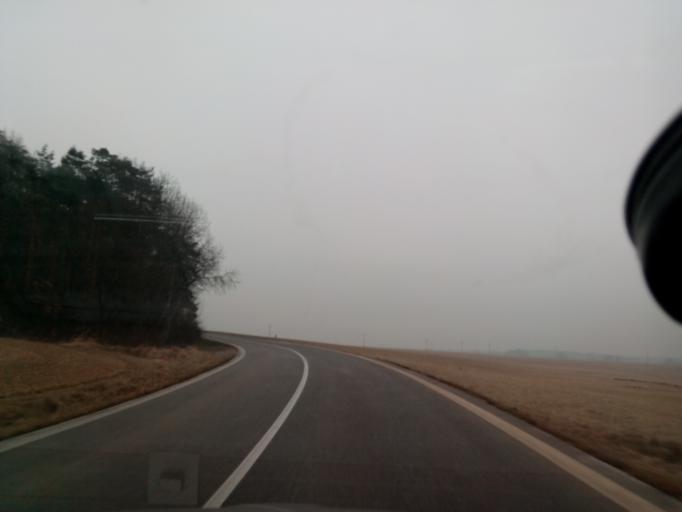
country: SK
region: Kosicky
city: Moldava nad Bodvou
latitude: 48.6789
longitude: 21.0822
